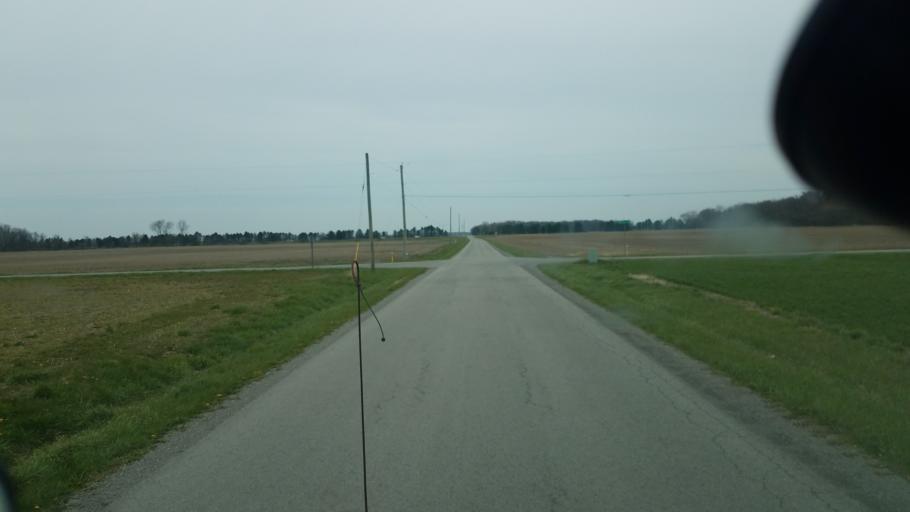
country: US
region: Ohio
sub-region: Wyandot County
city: Carey
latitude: 40.9753
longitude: -83.5128
